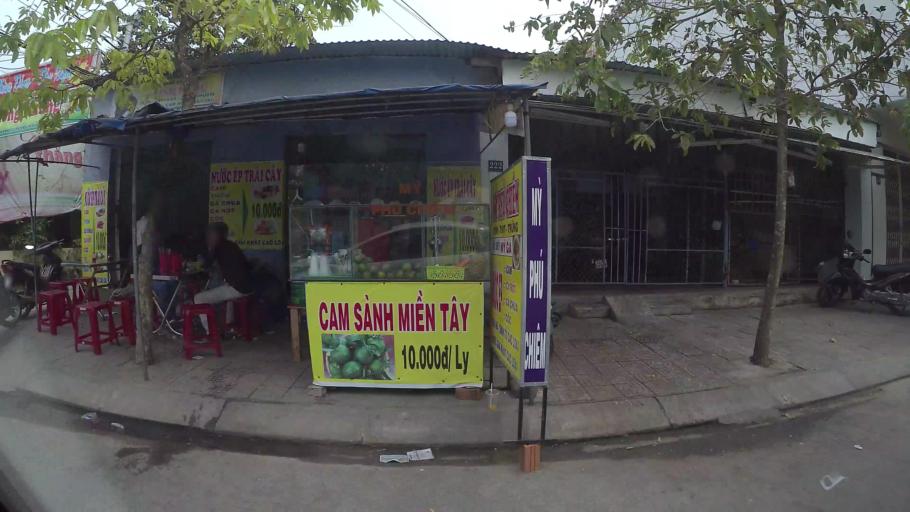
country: VN
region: Da Nang
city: Lien Chieu
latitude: 16.0655
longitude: 108.1669
